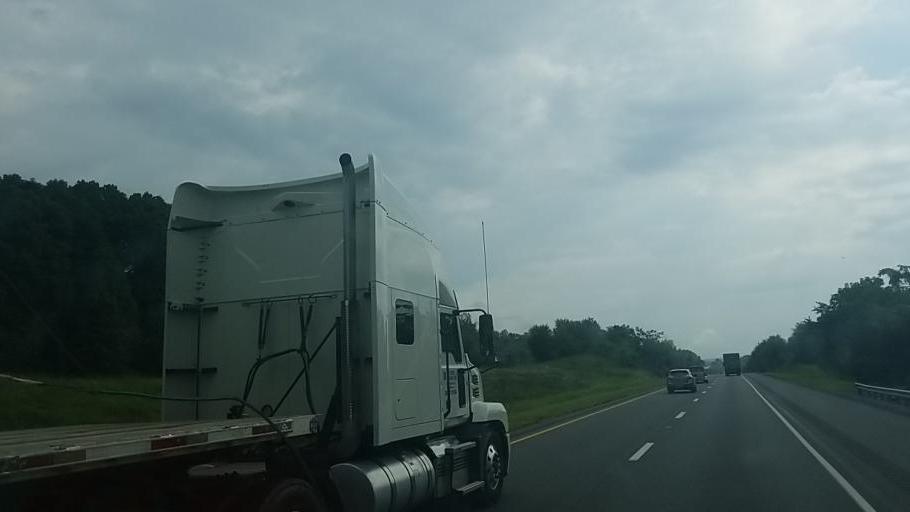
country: US
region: Pennsylvania
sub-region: Juniata County
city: Mifflintown
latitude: 40.5566
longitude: -77.2878
